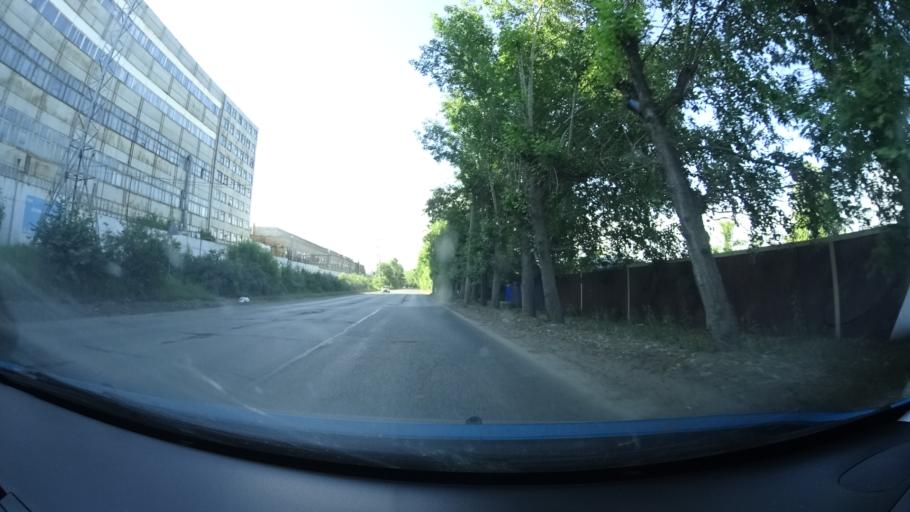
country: RU
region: Bashkortostan
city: Ufa
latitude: 54.8413
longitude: 56.0755
